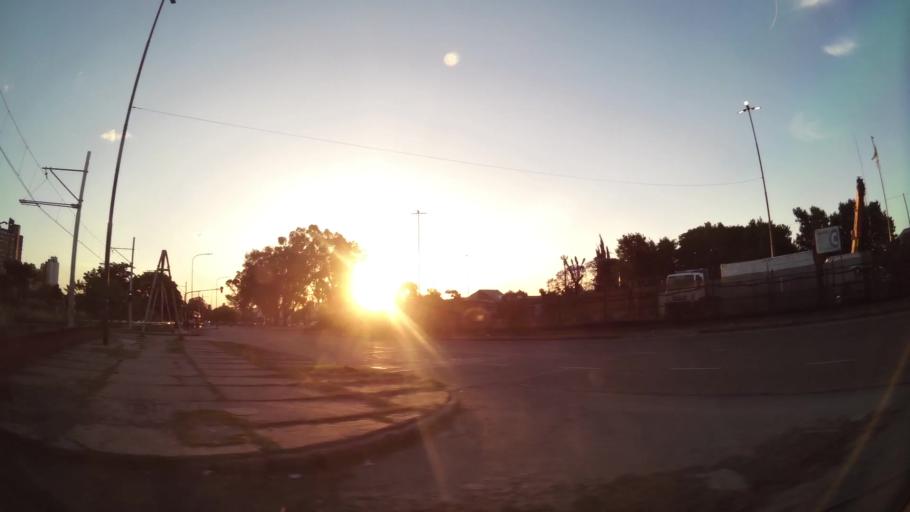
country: AR
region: Buenos Aires F.D.
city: Villa Lugano
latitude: -34.6799
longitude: -58.4661
